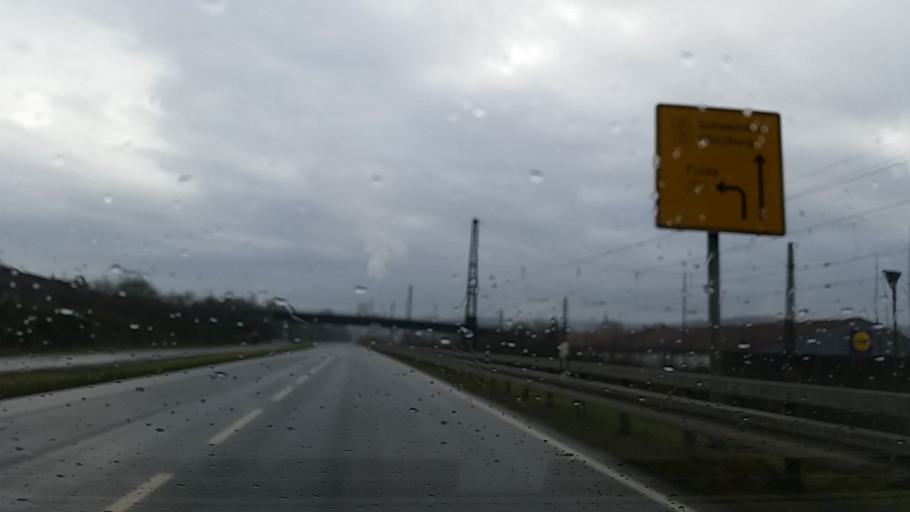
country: DE
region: Bavaria
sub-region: Regierungsbezirk Unterfranken
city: Karlstadt
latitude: 49.9680
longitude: 9.7682
